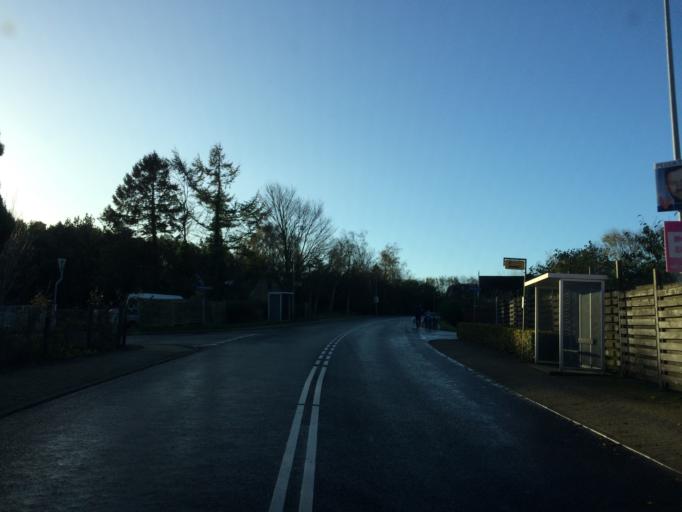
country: DK
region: South Denmark
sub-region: Fredericia Kommune
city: Taulov
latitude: 55.5434
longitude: 9.6128
